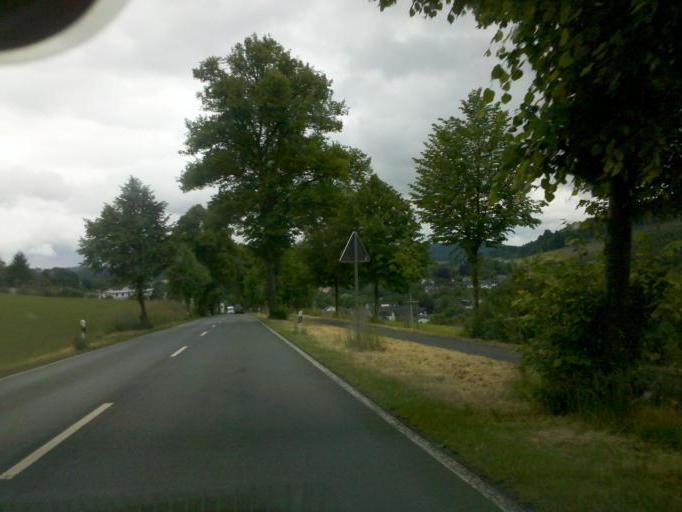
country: DE
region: North Rhine-Westphalia
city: Eslohe
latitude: 51.2608
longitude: 8.1805
